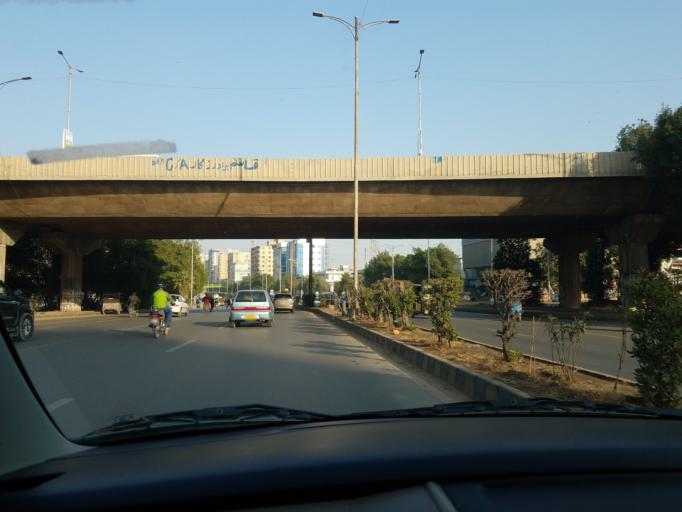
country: PK
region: Sindh
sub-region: Karachi District
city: Karachi
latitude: 24.8597
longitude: 67.0585
